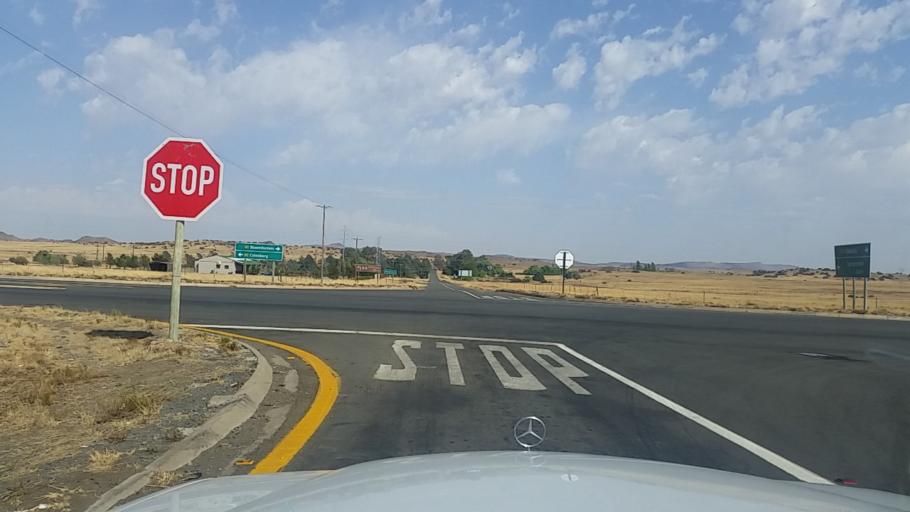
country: ZA
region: Orange Free State
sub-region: Xhariep District Municipality
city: Trompsburg
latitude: -30.2943
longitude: 25.7239
